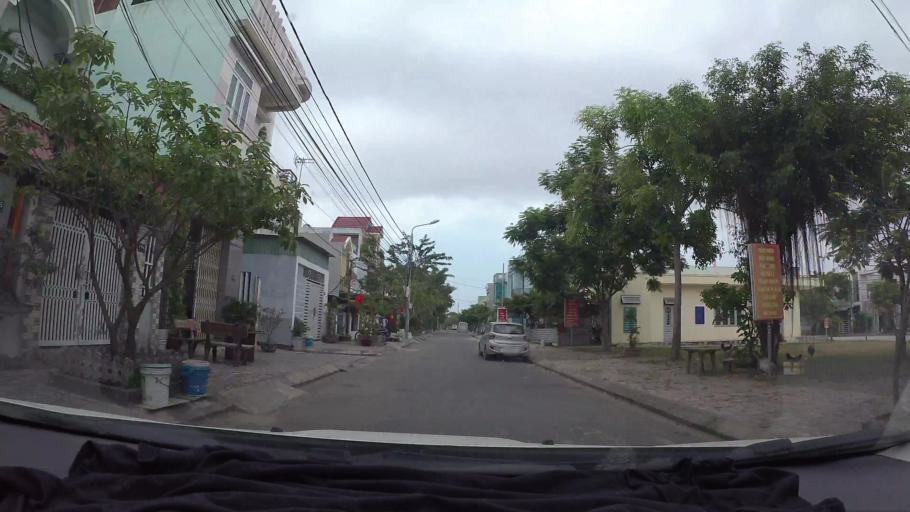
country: VN
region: Da Nang
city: Cam Le
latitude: 16.0362
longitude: 108.1745
